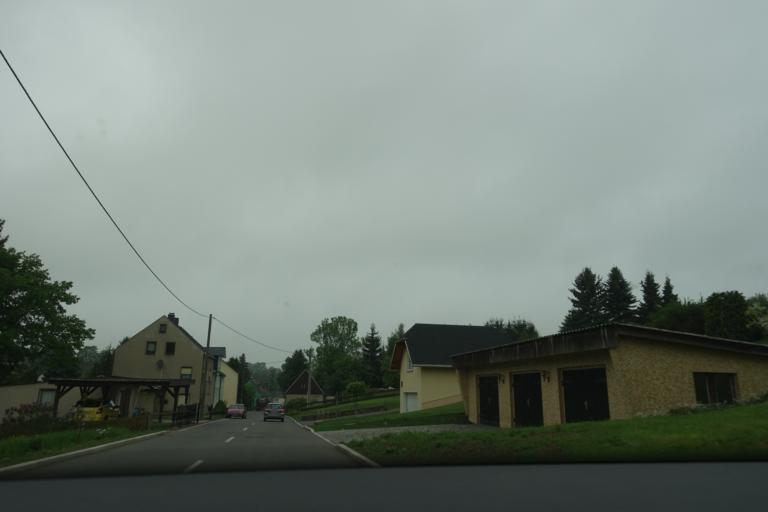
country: DE
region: Saxony
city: Brand-Erbisdorf
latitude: 50.8325
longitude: 13.2973
